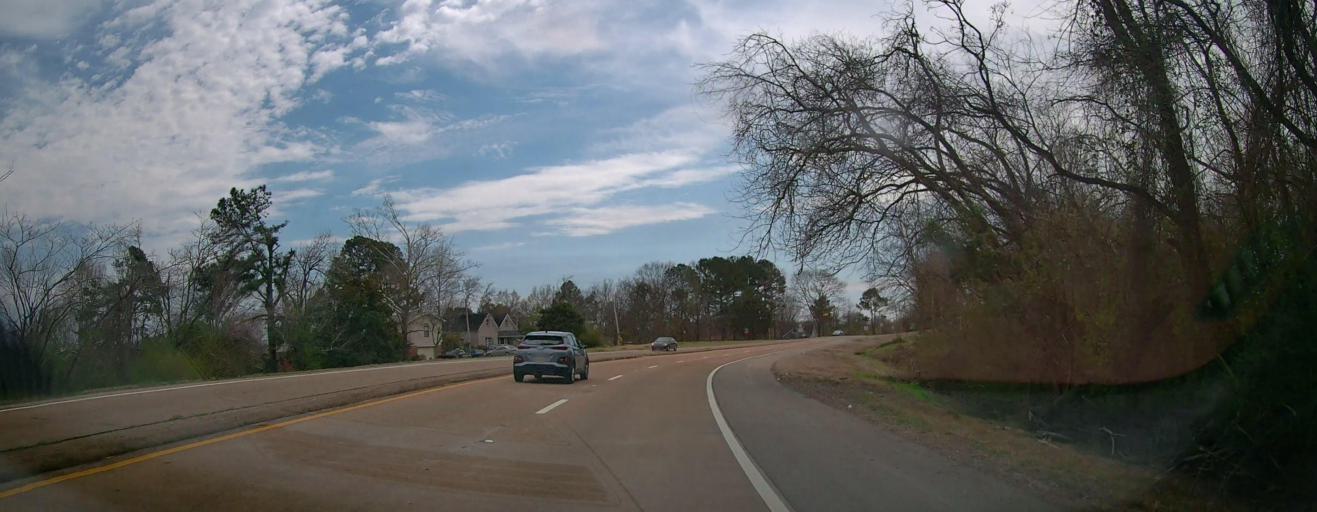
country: US
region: Mississippi
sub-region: Lee County
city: Tupelo
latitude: 34.2719
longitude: -88.7038
